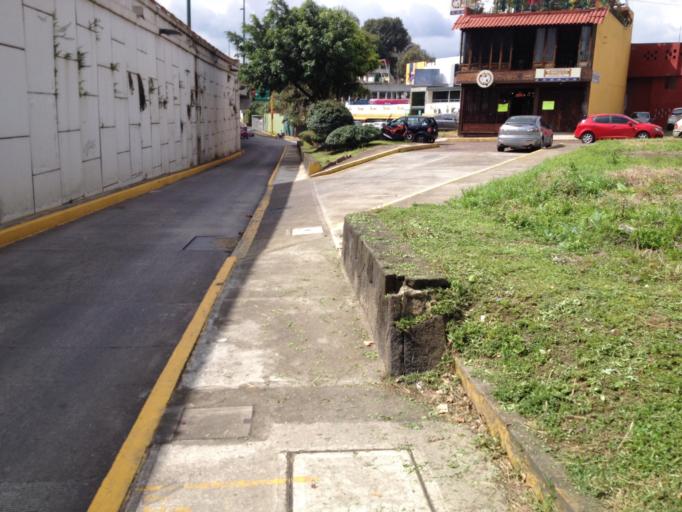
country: MX
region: Veracruz
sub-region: Xalapa
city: Xalapa de Enriquez
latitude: 19.5229
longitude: -96.9096
